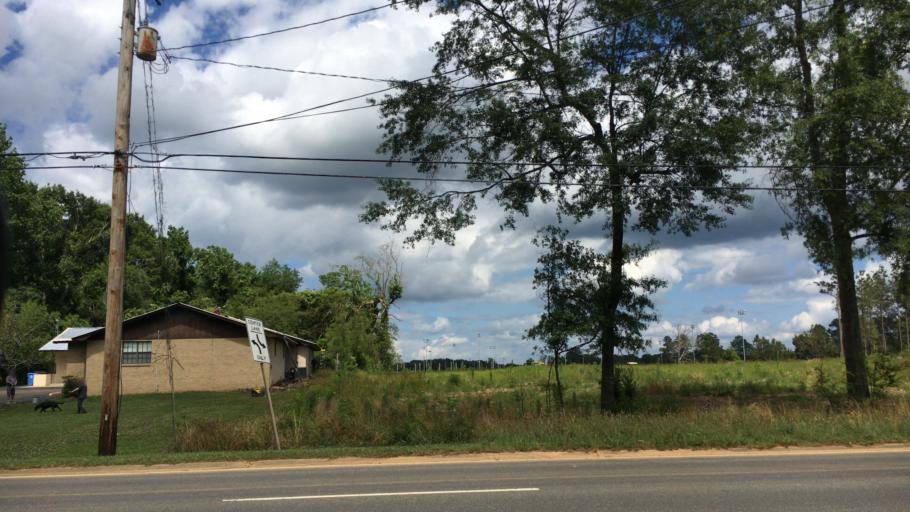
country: US
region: Louisiana
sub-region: Lincoln Parish
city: Ruston
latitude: 32.5081
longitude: -92.6374
